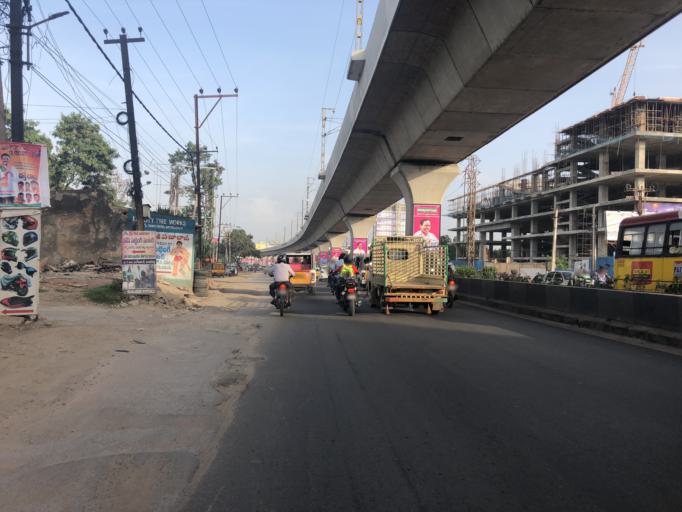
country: IN
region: Telangana
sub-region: Rangareddi
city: Kukatpalli
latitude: 17.4808
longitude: 78.4170
